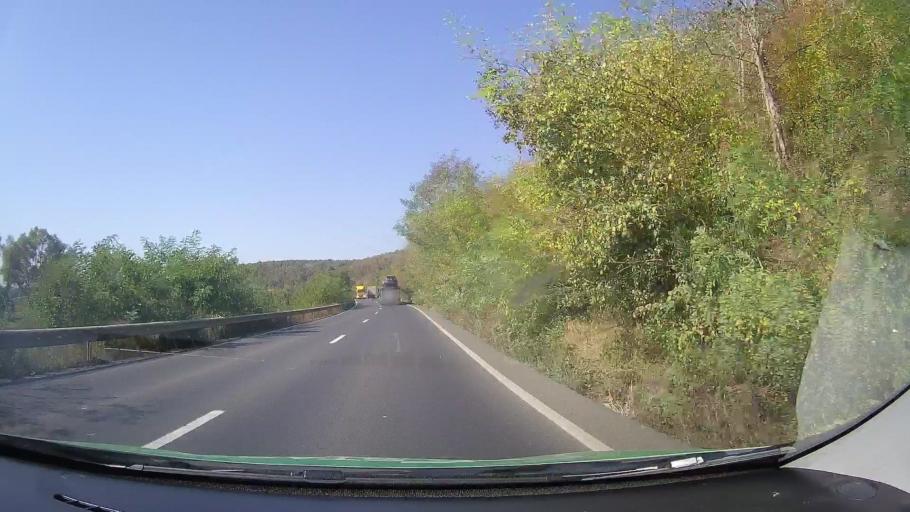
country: RO
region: Arad
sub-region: Comuna Bata
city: Bata
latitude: 46.0351
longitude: 22.0845
